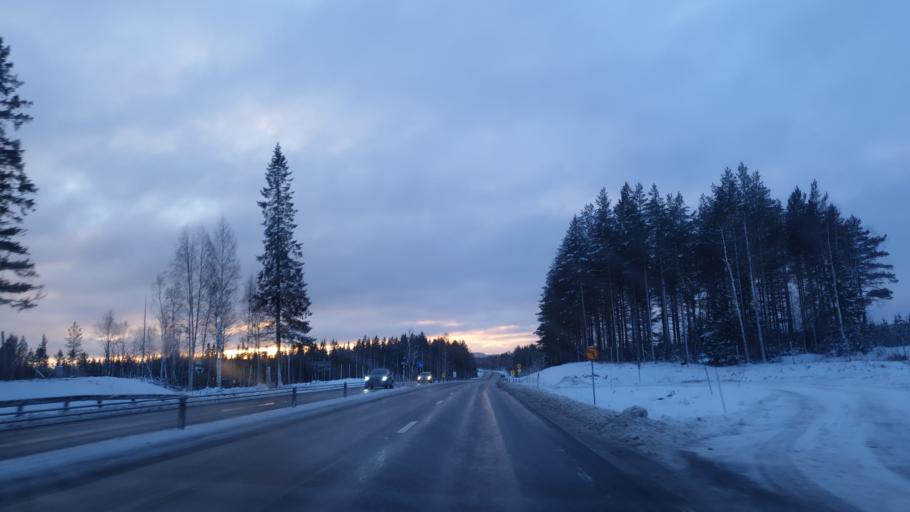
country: SE
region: Vaesternorrland
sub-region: OErnskoeldsviks Kommun
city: Husum
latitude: 63.4869
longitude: 19.3076
